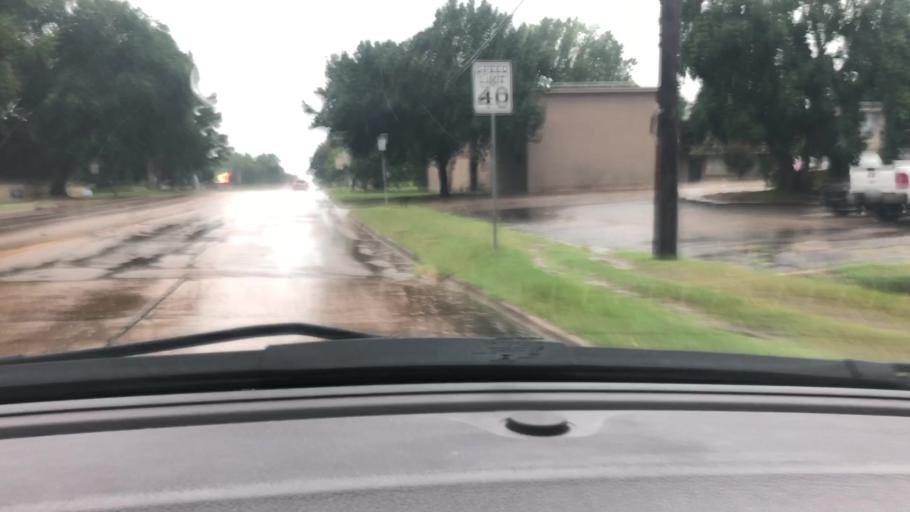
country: US
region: Texas
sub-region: Bowie County
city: Wake Village
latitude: 33.4456
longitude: -94.0804
